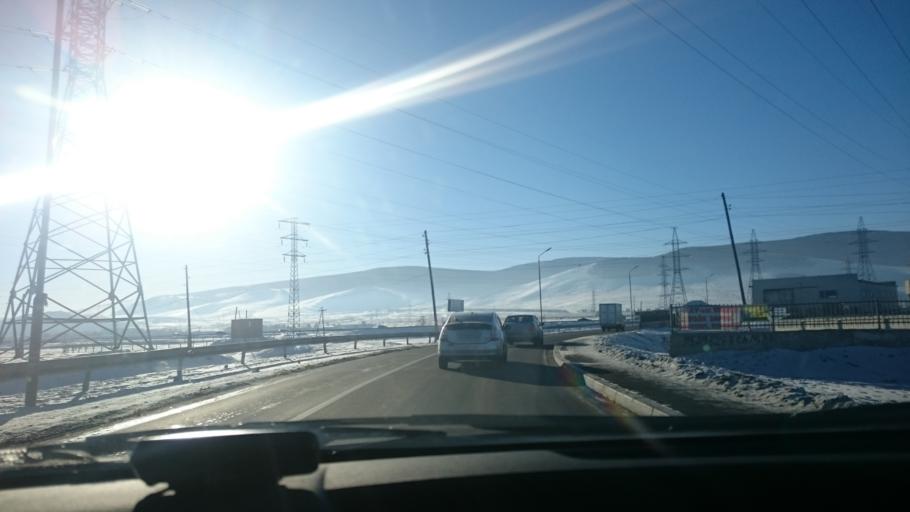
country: MN
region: Ulaanbaatar
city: Ulaanbaatar
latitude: 47.9025
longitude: 107.0355
